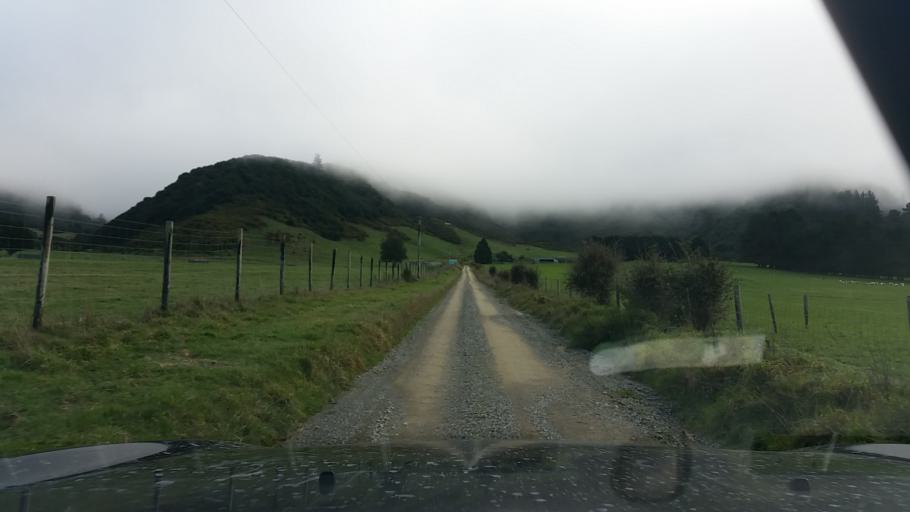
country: NZ
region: Marlborough
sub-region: Marlborough District
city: Picton
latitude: -41.1719
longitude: 173.9660
